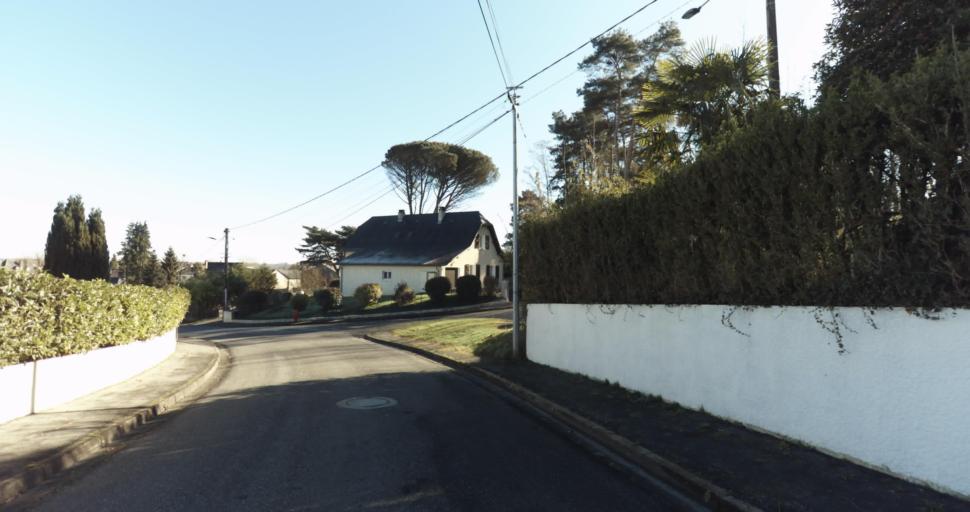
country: FR
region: Aquitaine
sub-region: Departement des Pyrenees-Atlantiques
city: Morlaas
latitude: 43.3425
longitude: -0.2691
